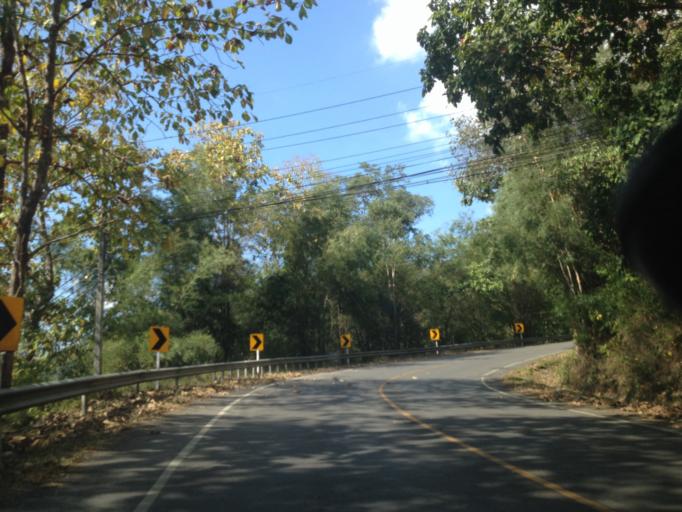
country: TH
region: Chiang Mai
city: Samoeng
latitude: 18.8509
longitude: 98.7518
